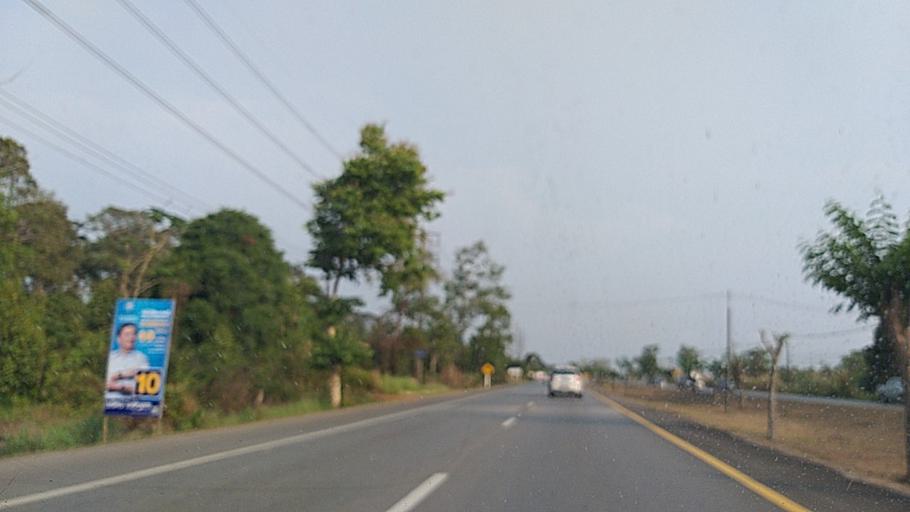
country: TH
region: Chanthaburi
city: Khlung
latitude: 12.4505
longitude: 102.2856
